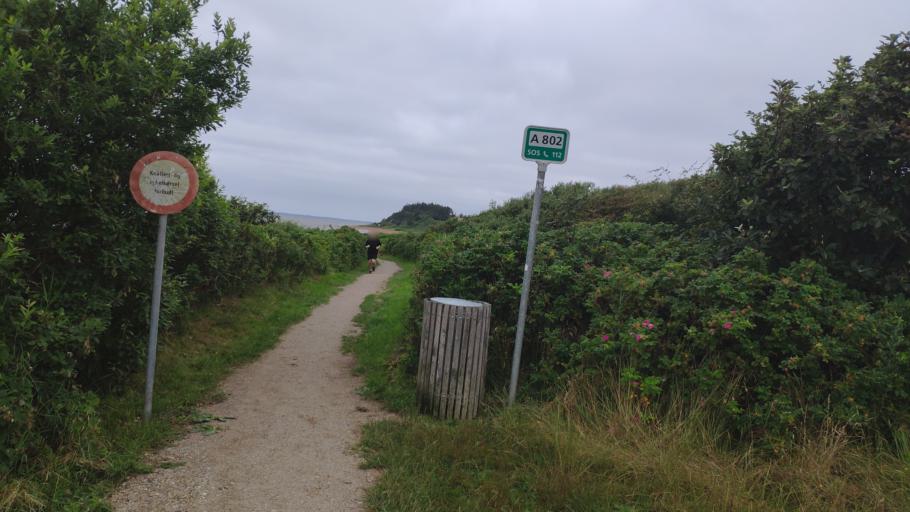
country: DK
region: South Denmark
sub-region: Fano Kommune
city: Nordby
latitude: 55.5323
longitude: 8.3425
